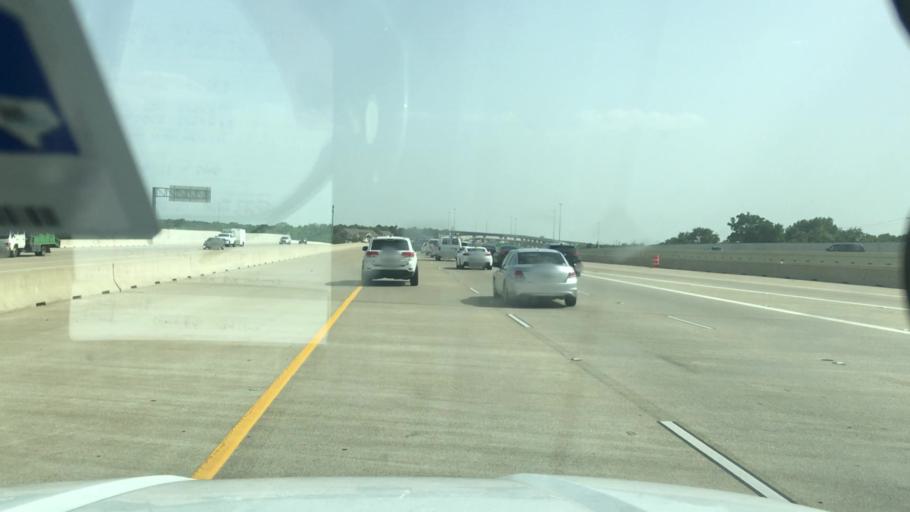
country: US
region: Texas
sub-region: Dallas County
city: Grand Prairie
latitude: 32.7740
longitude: -97.0272
